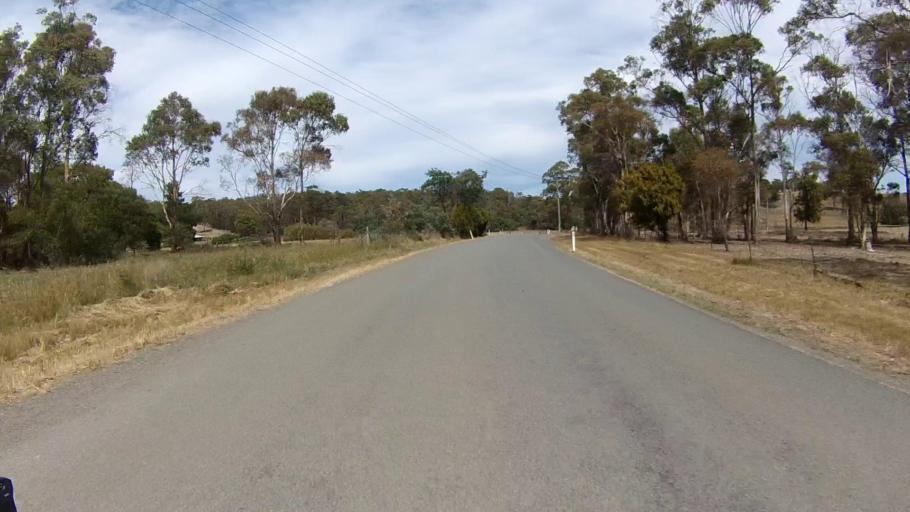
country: AU
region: Tasmania
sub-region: Sorell
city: Sorell
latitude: -42.8032
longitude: 147.6445
